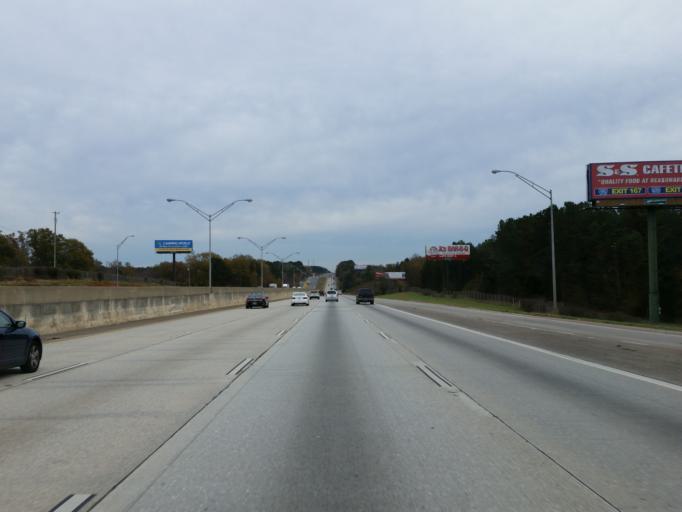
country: US
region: Georgia
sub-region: Monroe County
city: Forsyth
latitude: 33.0263
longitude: -83.9068
